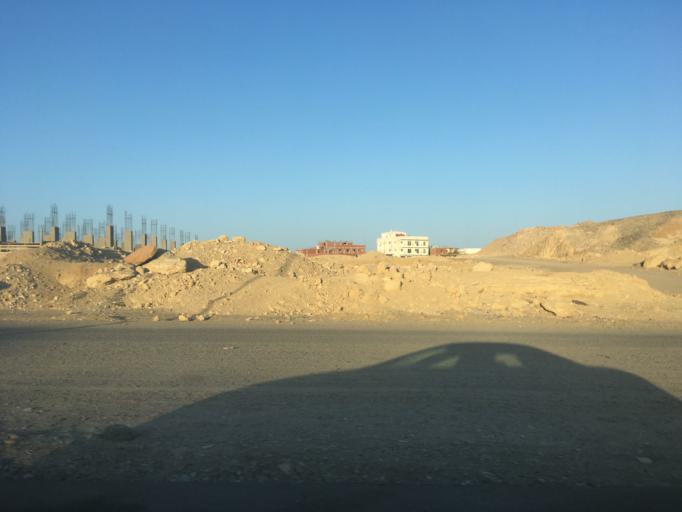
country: EG
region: Red Sea
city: Marsa Alam
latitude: 25.0752
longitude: 34.8858
